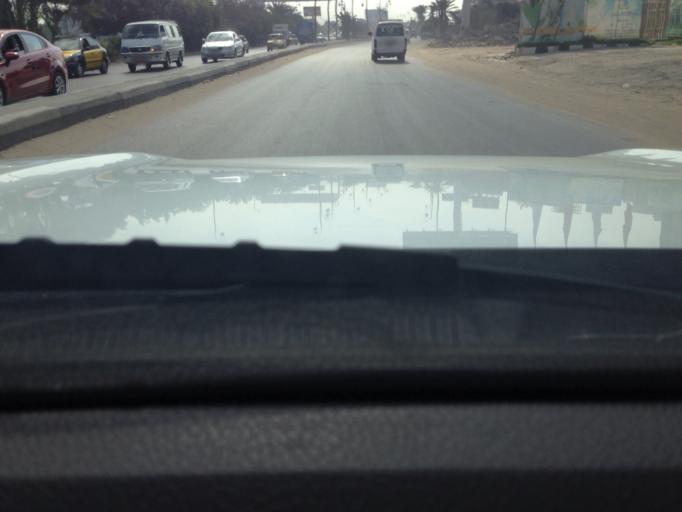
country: EG
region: Alexandria
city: Alexandria
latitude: 31.2037
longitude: 29.9854
